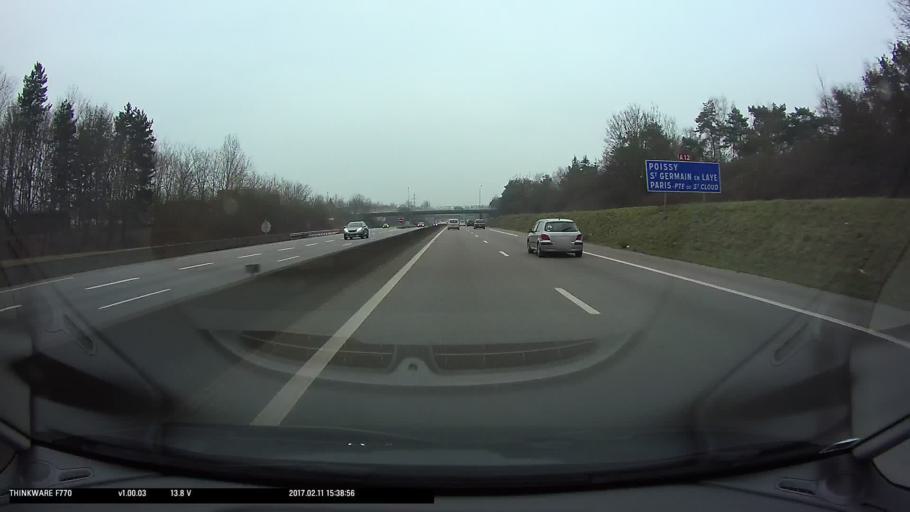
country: FR
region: Ile-de-France
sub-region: Departement des Yvelines
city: Bois-d'Arcy
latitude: 48.7900
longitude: 2.0382
